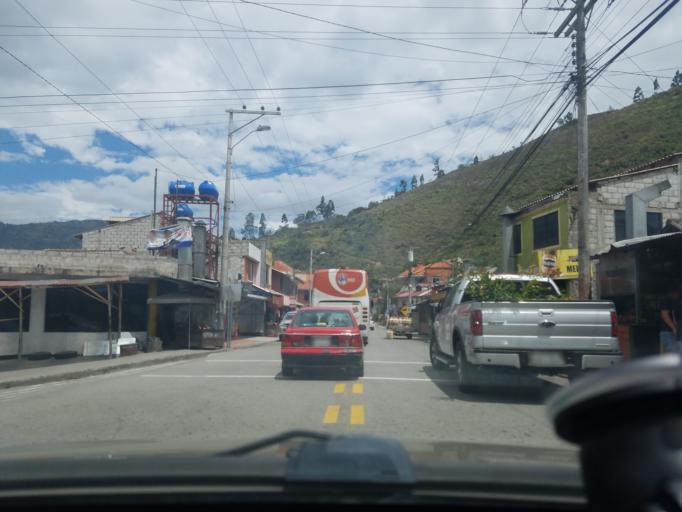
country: EC
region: Azuay
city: La Union
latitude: -2.8532
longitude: -78.7792
